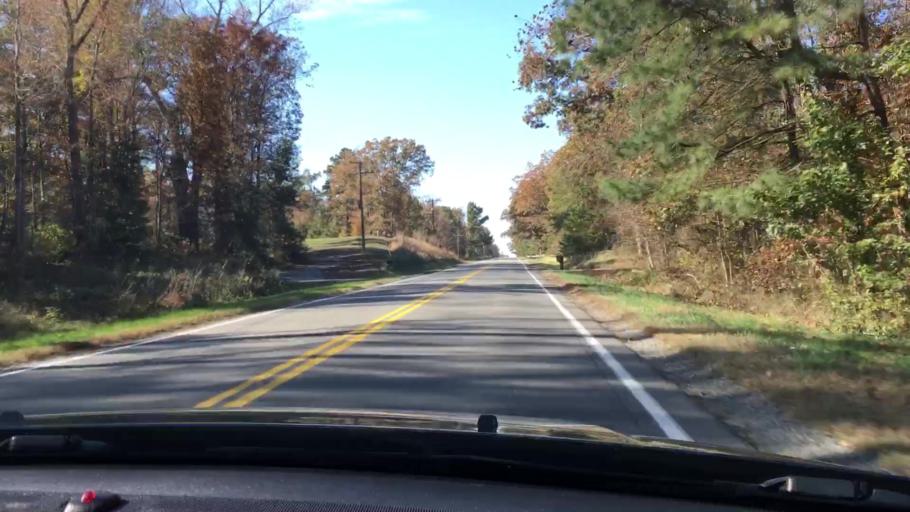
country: US
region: Virginia
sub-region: King William County
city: King William
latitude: 37.7145
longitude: -77.0652
